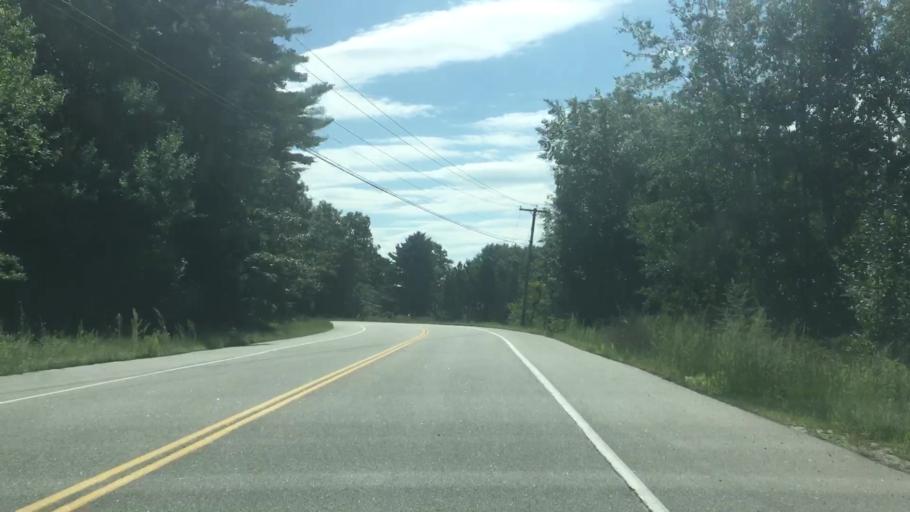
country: US
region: Maine
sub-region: Androscoggin County
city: Lewiston
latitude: 44.0836
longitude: -70.1776
